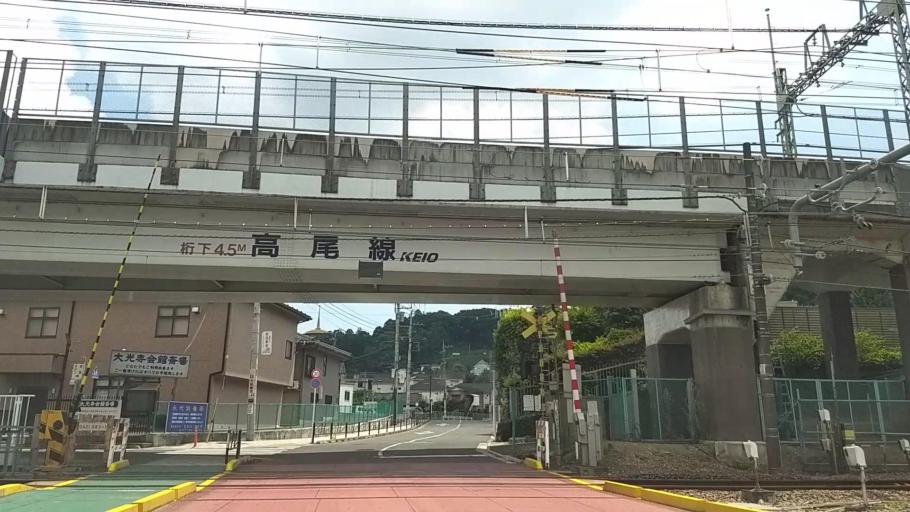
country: JP
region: Tokyo
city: Hachioji
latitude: 35.6416
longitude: 139.2803
